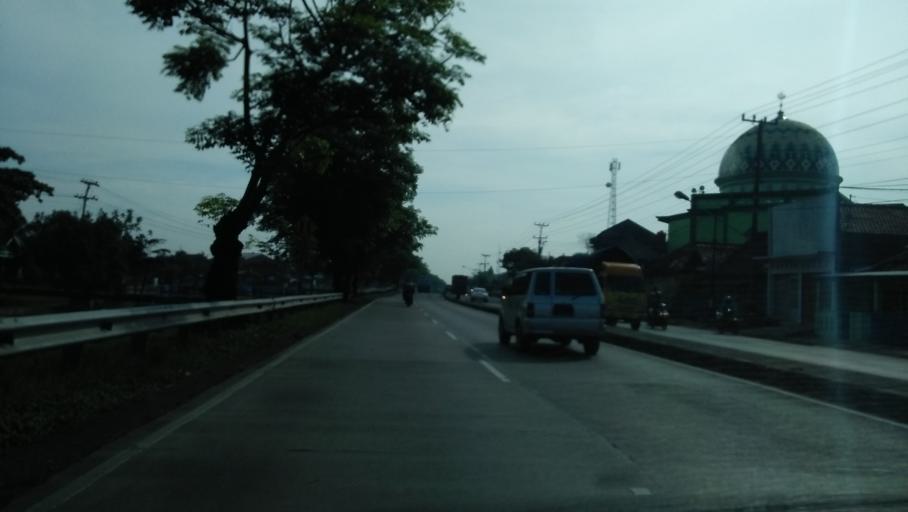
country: ID
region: Central Java
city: Demak
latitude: -6.9277
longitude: 110.5518
